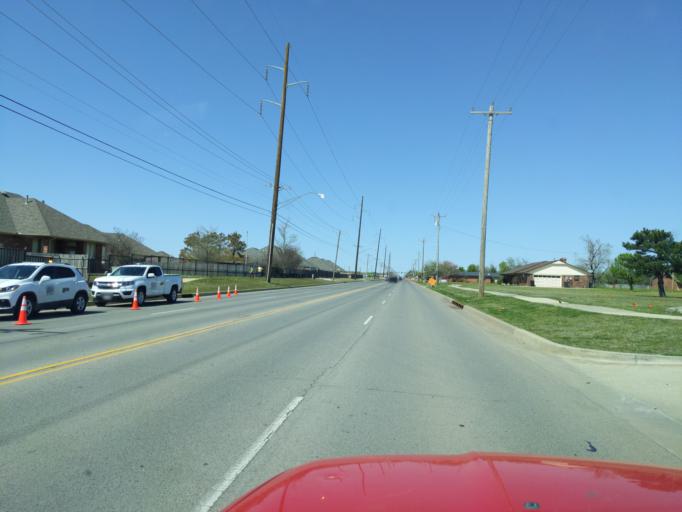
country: US
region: Oklahoma
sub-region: Cleveland County
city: Moore
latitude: 35.3295
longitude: -97.5120
